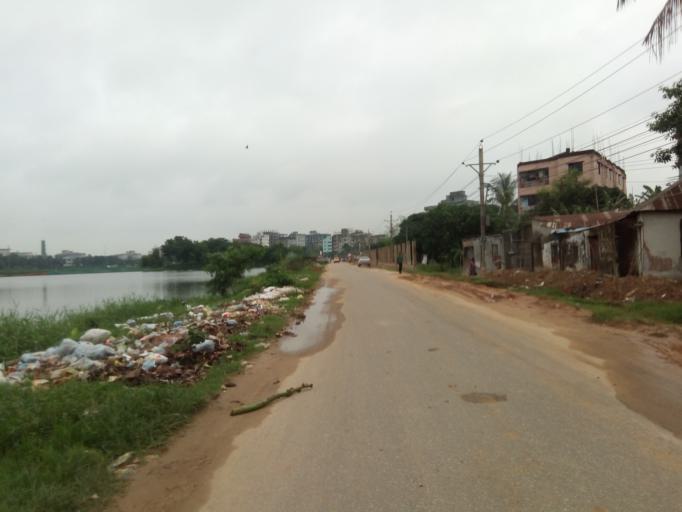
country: BD
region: Dhaka
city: Tungi
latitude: 23.8478
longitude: 90.4175
